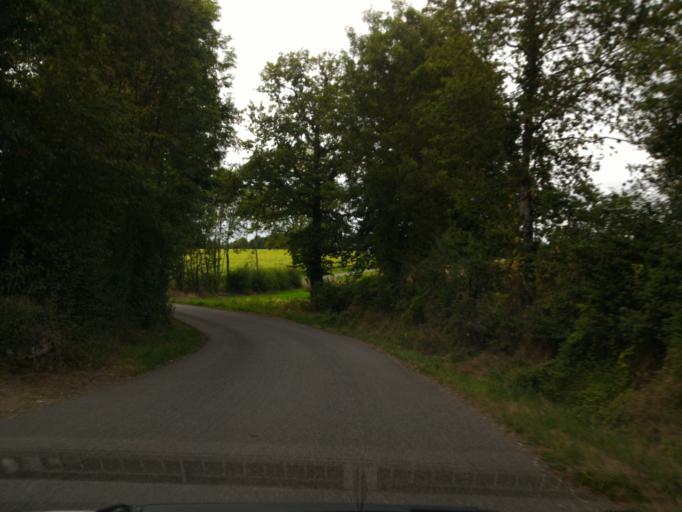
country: FR
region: Poitou-Charentes
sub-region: Departement de la Charente
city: Brigueuil
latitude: 45.9295
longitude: 0.8286
